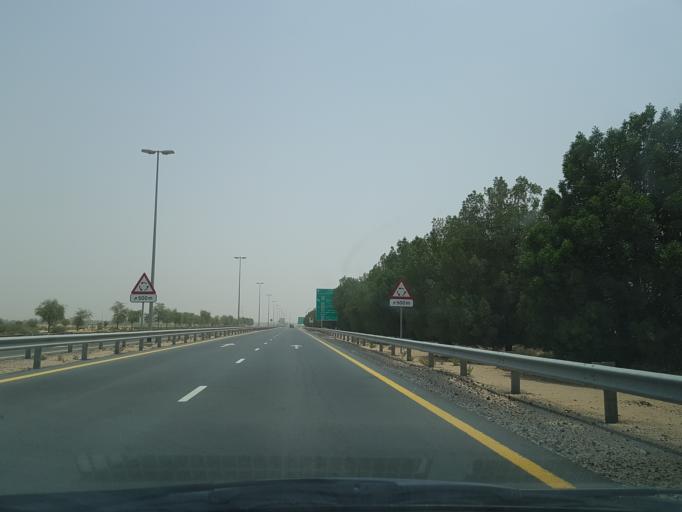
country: AE
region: Dubai
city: Dubai
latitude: 24.8485
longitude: 55.3403
